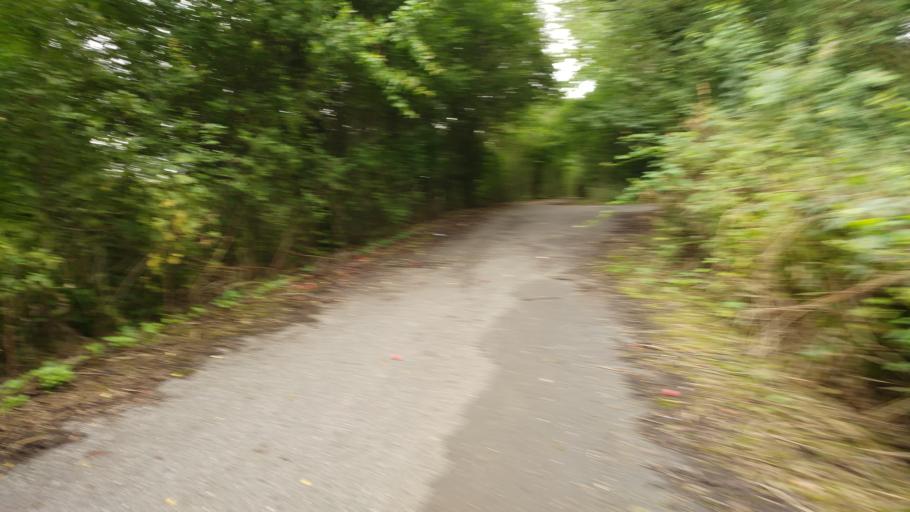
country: CZ
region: Central Bohemia
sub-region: Okres Praha-Zapad
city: Pruhonice
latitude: 50.0358
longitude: 14.5378
